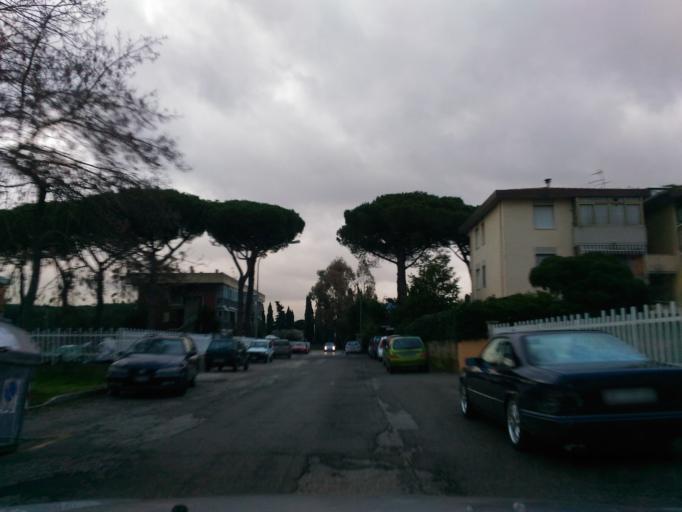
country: IT
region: Tuscany
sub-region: Provincia di Livorno
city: Guasticce
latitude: 43.5906
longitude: 10.3560
